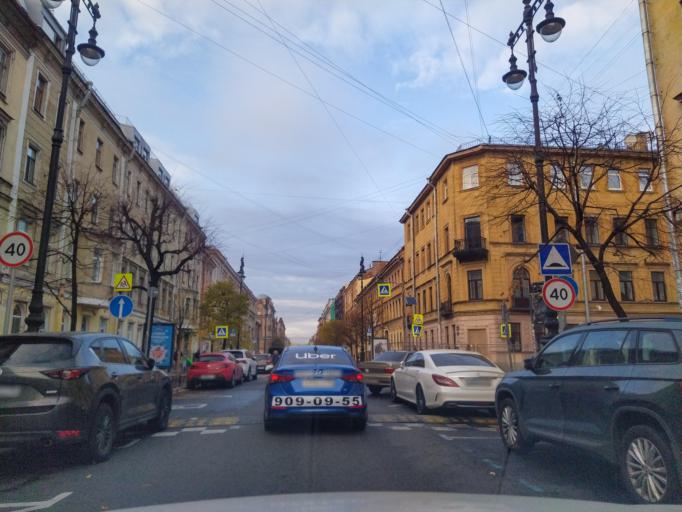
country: RU
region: St.-Petersburg
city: Centralniy
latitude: 59.9370
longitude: 30.3551
